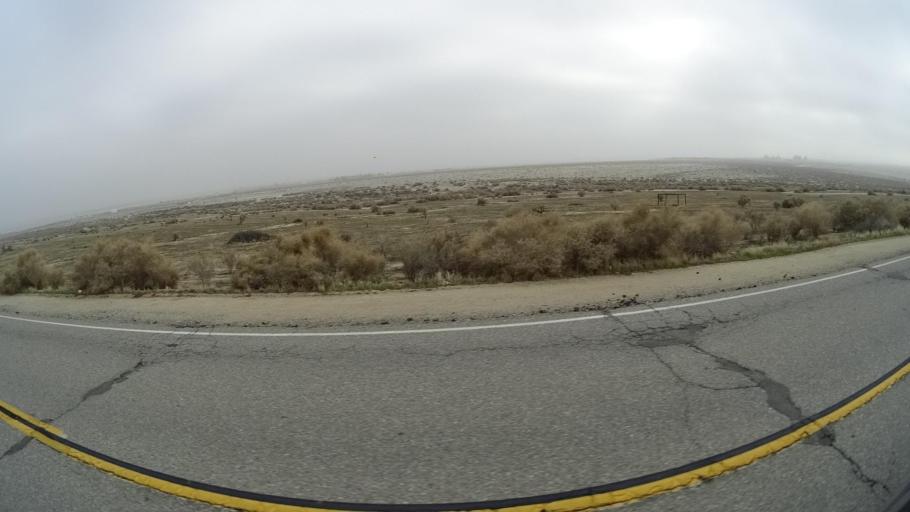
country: US
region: California
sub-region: Kern County
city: South Taft
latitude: 35.1301
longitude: -119.3868
